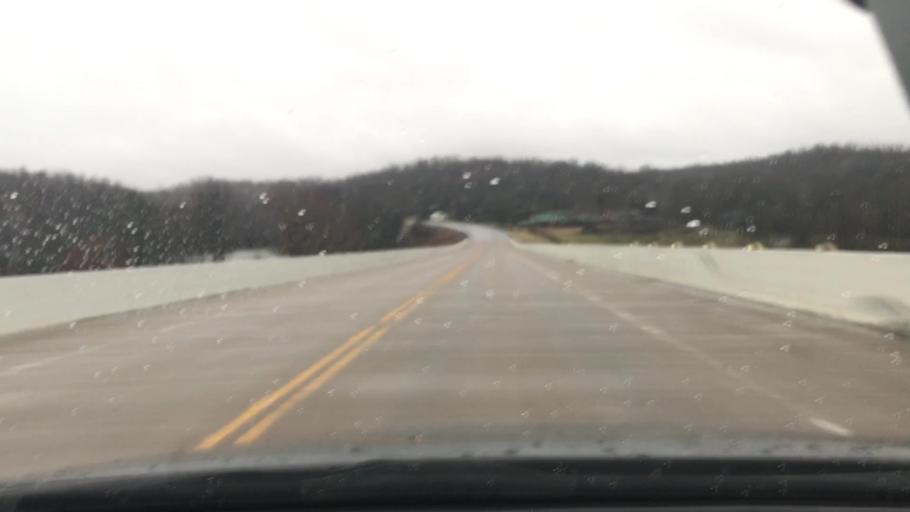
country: US
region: Tennessee
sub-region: Cheatham County
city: Ashland City
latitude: 36.2855
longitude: -87.1465
